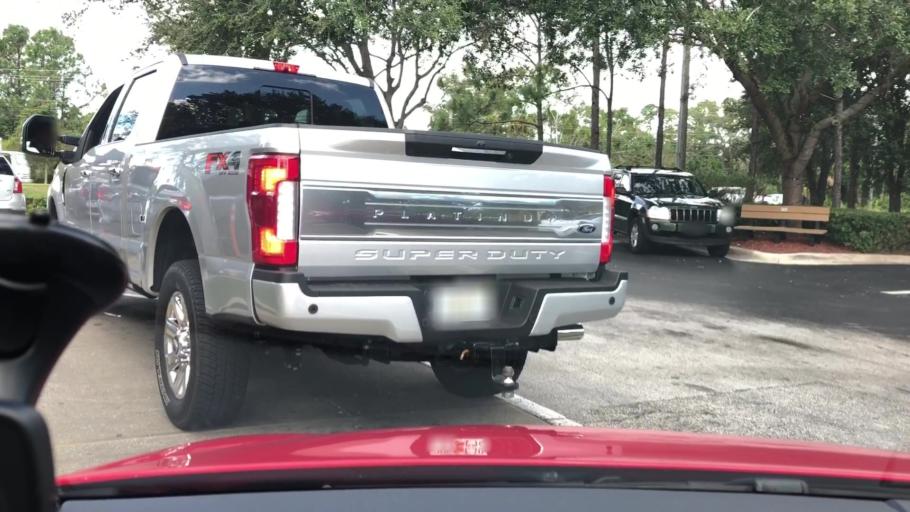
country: US
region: Florida
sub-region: Volusia County
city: Ormond Beach
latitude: 29.2582
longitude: -81.1108
